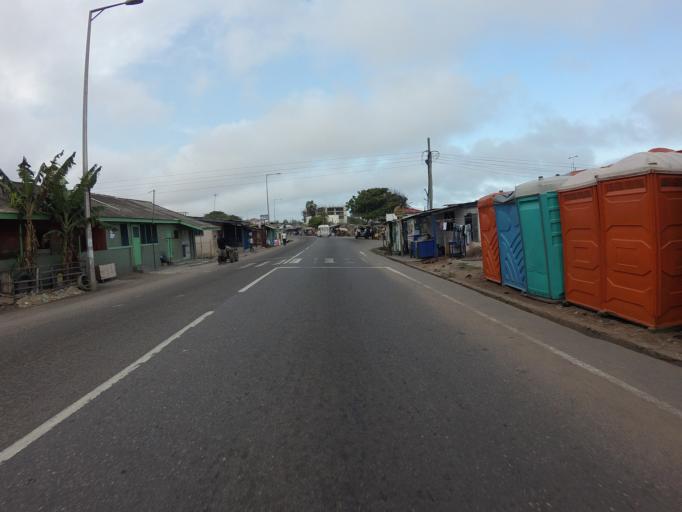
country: GH
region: Greater Accra
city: Accra
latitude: 5.5507
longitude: -0.1825
